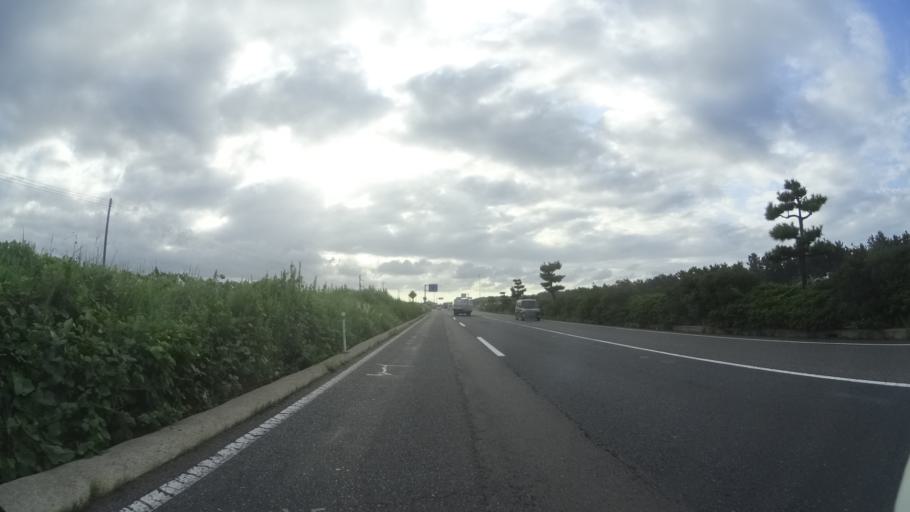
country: JP
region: Tottori
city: Kurayoshi
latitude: 35.4984
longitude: 133.7758
